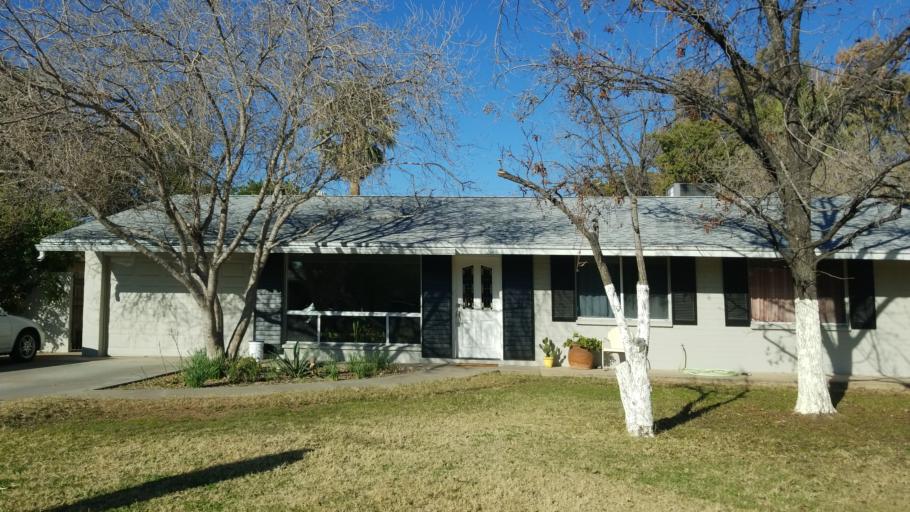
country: US
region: Arizona
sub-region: Maricopa County
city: Glendale
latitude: 33.5516
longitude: -112.0962
